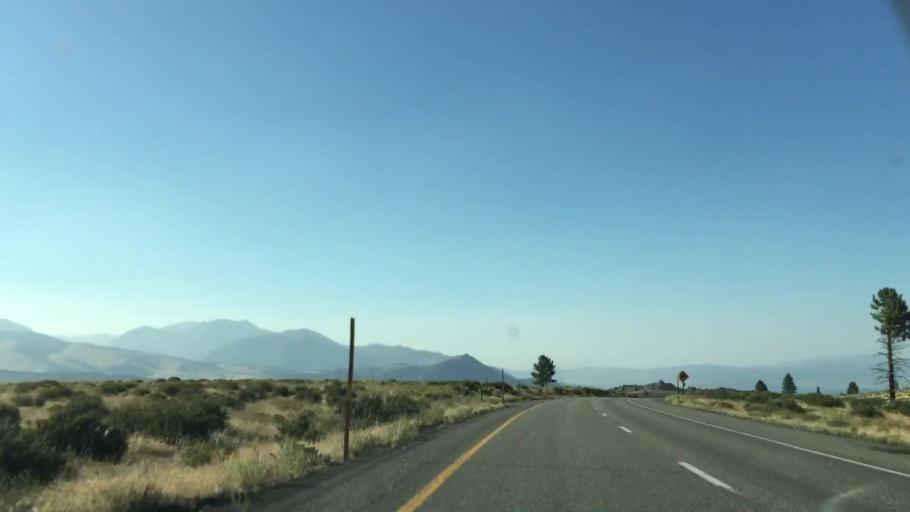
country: US
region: California
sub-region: Mono County
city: Mammoth Lakes
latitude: 37.8326
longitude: -119.0690
